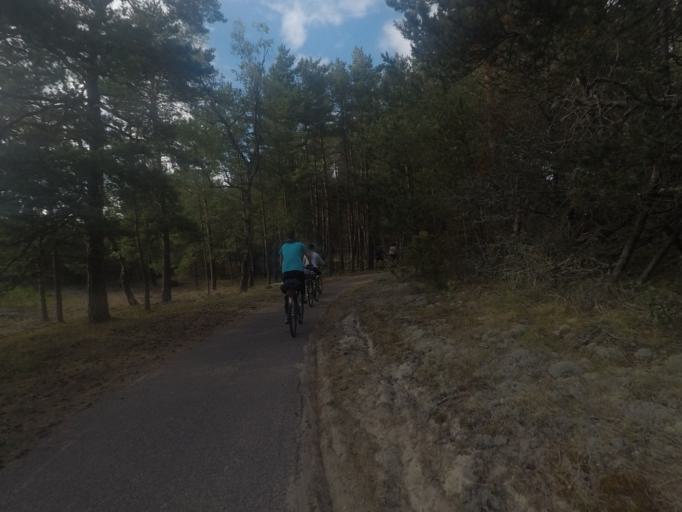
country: LT
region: Klaipedos apskritis
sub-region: Klaipeda
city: Klaipeda
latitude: 55.6256
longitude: 21.1189
